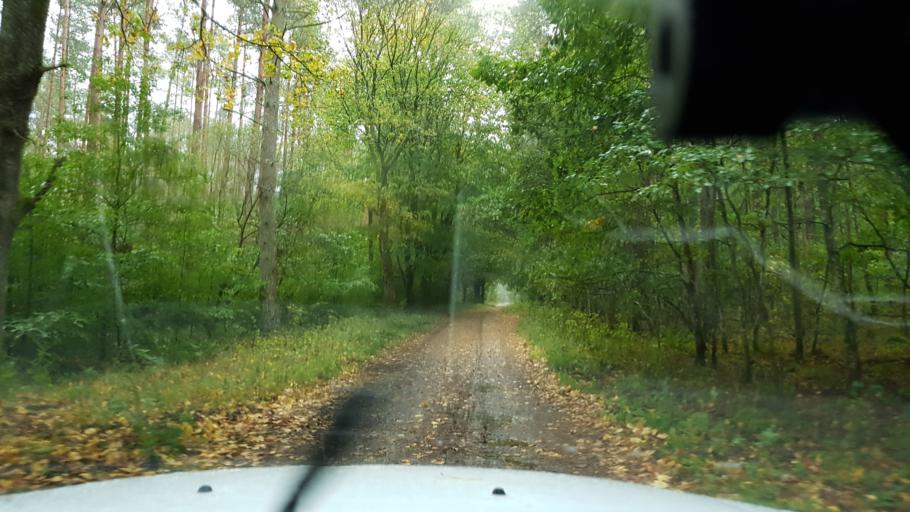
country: PL
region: West Pomeranian Voivodeship
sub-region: Powiat goleniowski
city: Przybiernow
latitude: 53.7386
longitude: 14.7983
